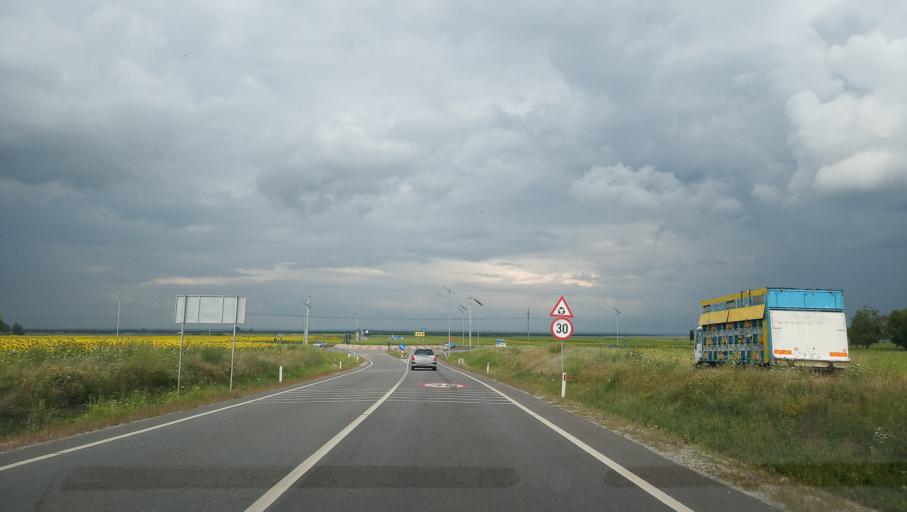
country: RO
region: Olt
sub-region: Comuna Deveselu
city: Comanca
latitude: 44.0891
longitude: 24.3639
